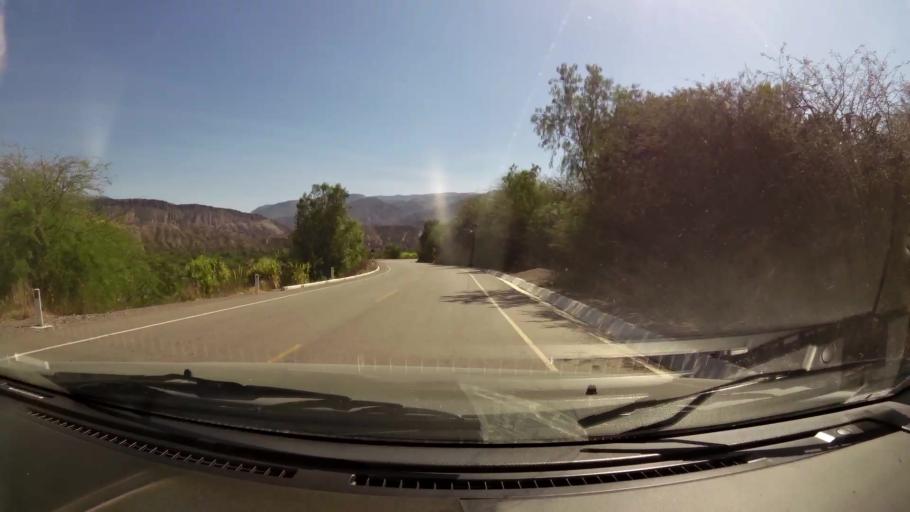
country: PE
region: Ayacucho
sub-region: Provincia de Huanta
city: Huanta
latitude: -12.9073
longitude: -74.3104
